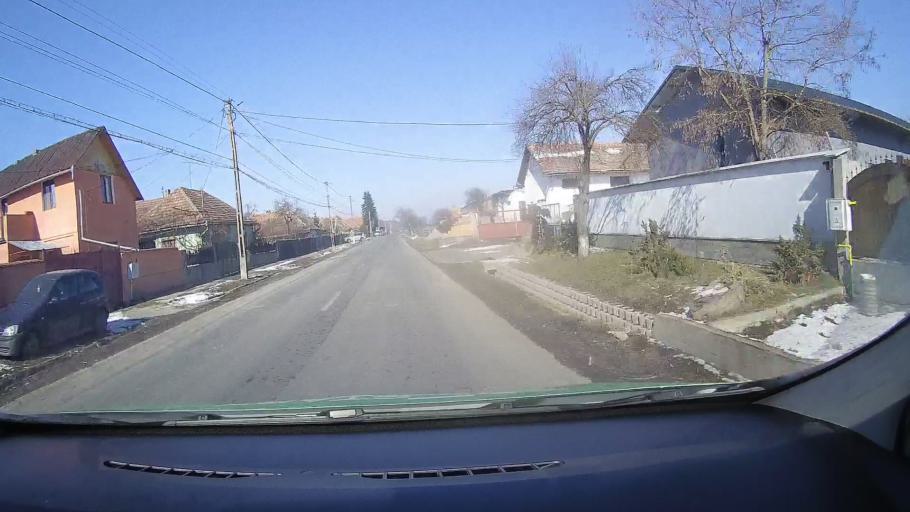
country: RO
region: Brasov
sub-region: Comuna Homorod
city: Homorod
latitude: 46.0206
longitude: 25.2746
